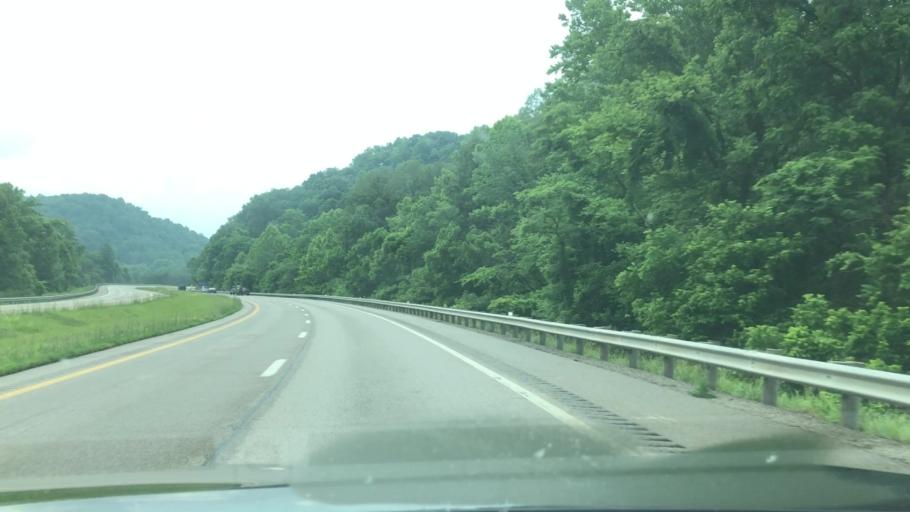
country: US
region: Ohio
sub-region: Jackson County
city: Jackson
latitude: 39.1512
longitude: -82.7287
